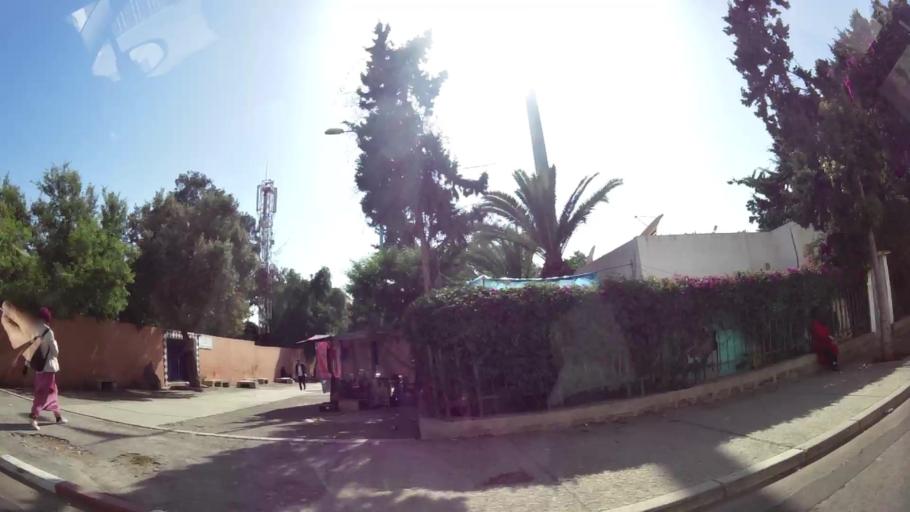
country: MA
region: Souss-Massa-Draa
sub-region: Agadir-Ida-ou-Tnan
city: Agadir
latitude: 30.4127
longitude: -9.5858
